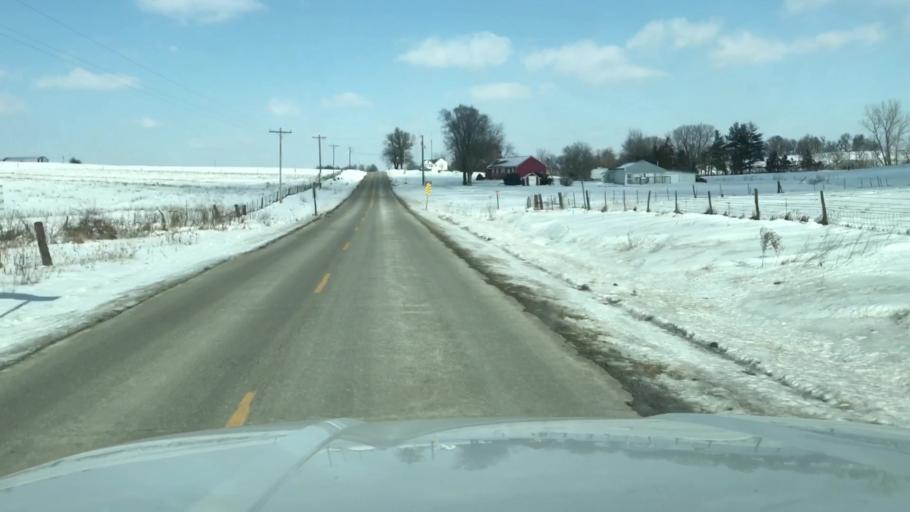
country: US
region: Missouri
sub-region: Nodaway County
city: Maryville
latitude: 40.3449
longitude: -94.7225
